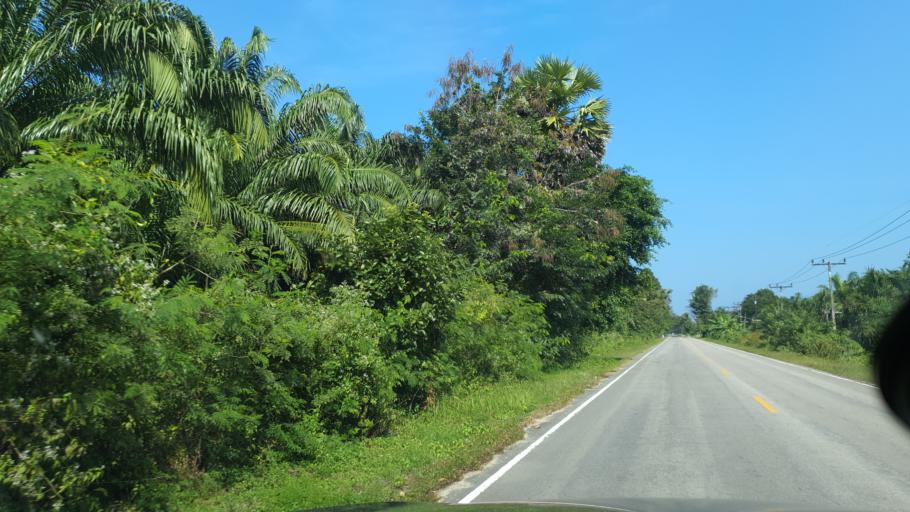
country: TH
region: Surat Thani
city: Tha Chana
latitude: 9.5786
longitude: 99.1884
